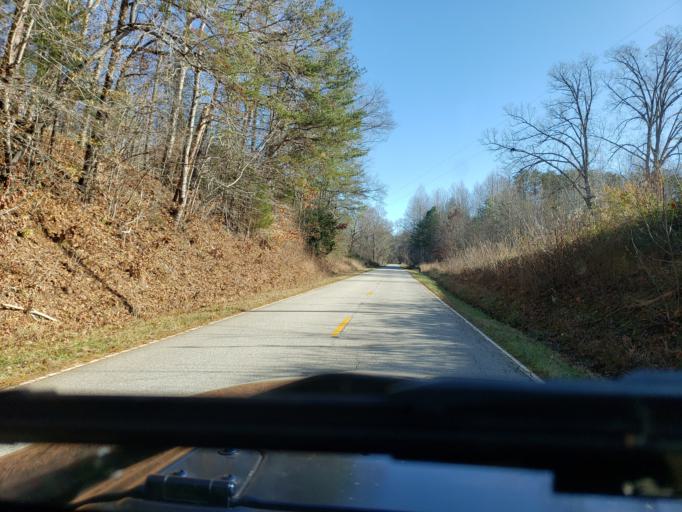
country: US
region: North Carolina
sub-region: Cleveland County
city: White Plains
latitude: 35.1553
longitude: -81.3991
